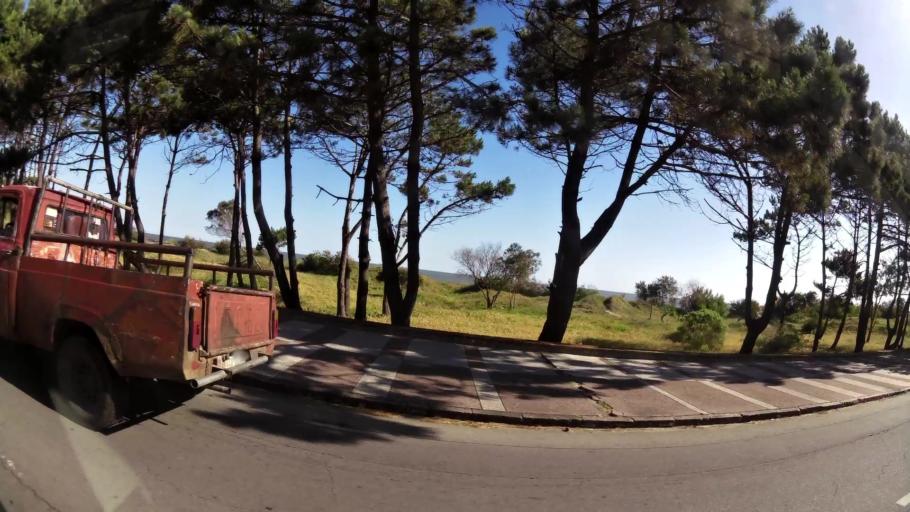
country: UY
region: Canelones
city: Paso de Carrasco
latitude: -34.8969
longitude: -56.0749
